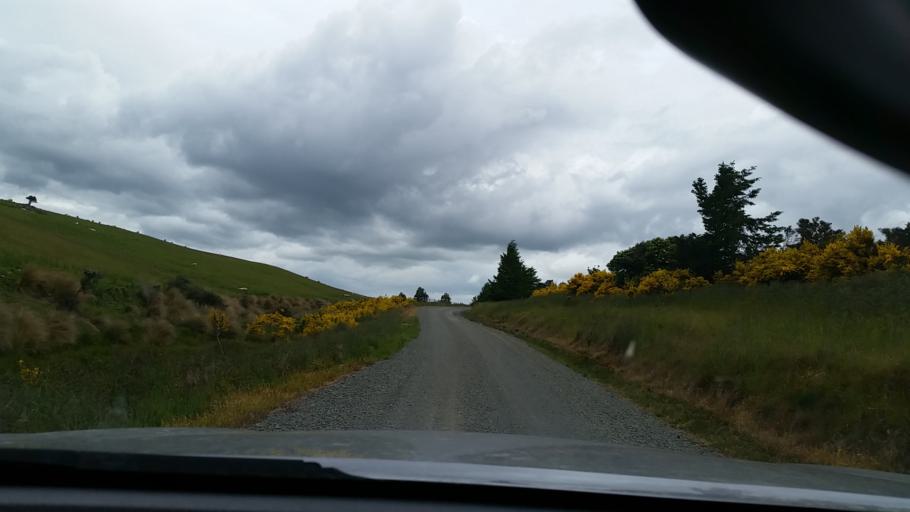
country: NZ
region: Southland
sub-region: Southland District
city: Winton
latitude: -45.8240
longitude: 168.1692
